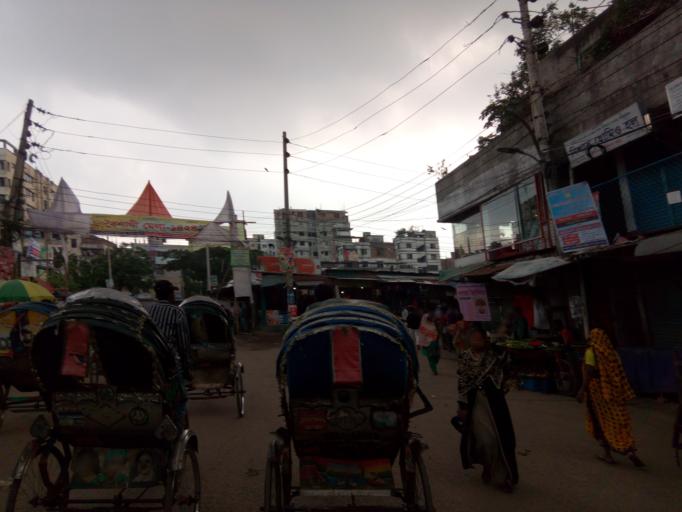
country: BD
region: Dhaka
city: Paltan
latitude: 23.7227
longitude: 90.4327
